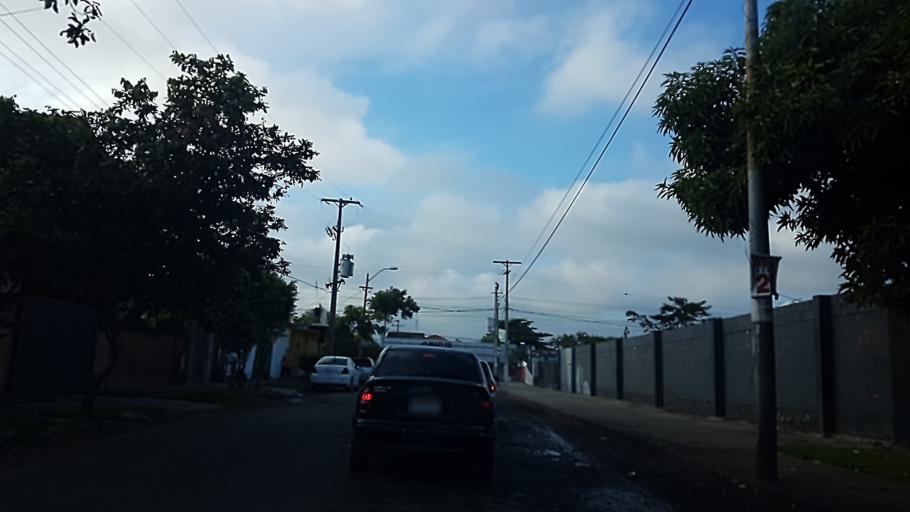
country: PY
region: Central
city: Fernando de la Mora
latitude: -25.2762
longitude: -57.5508
